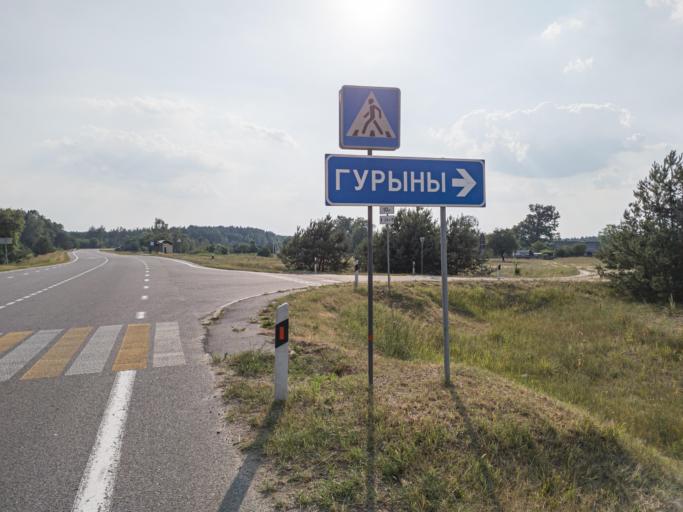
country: BY
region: Brest
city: Zhabinka
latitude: 52.3992
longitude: 24.0682
